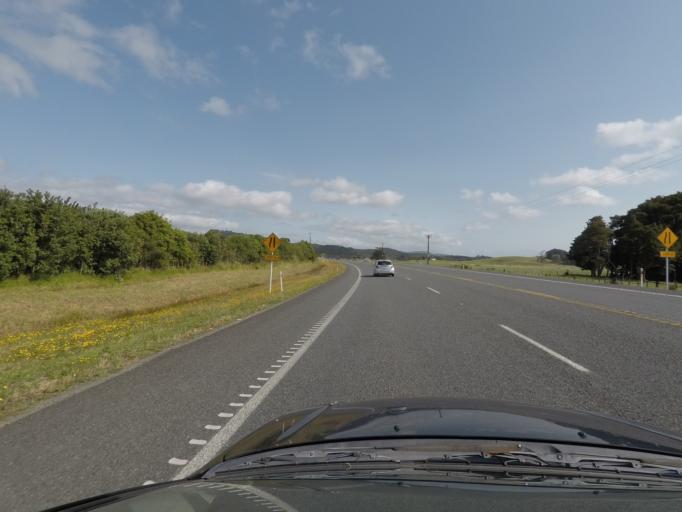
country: NZ
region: Northland
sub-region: Whangarei
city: Ruakaka
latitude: -36.0105
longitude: 174.4178
